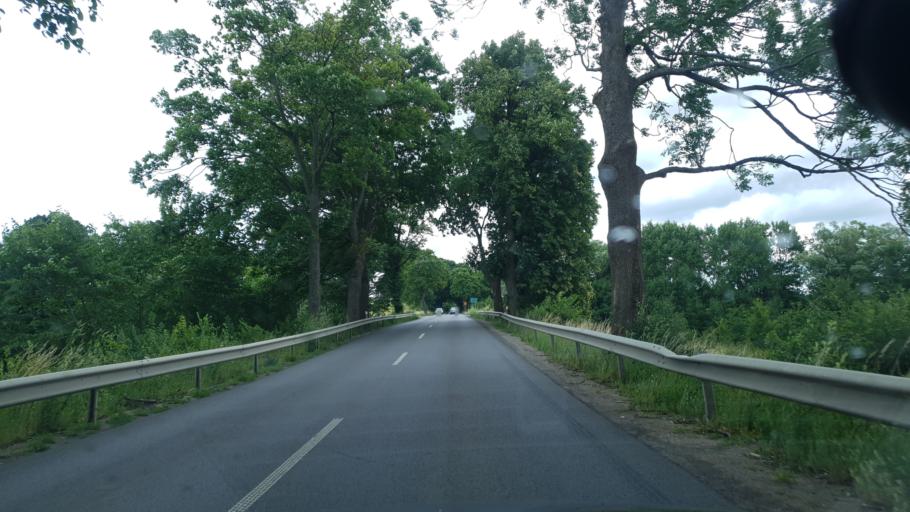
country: PL
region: Pomeranian Voivodeship
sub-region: Powiat kartuski
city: Zukowo
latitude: 54.3852
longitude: 18.3426
